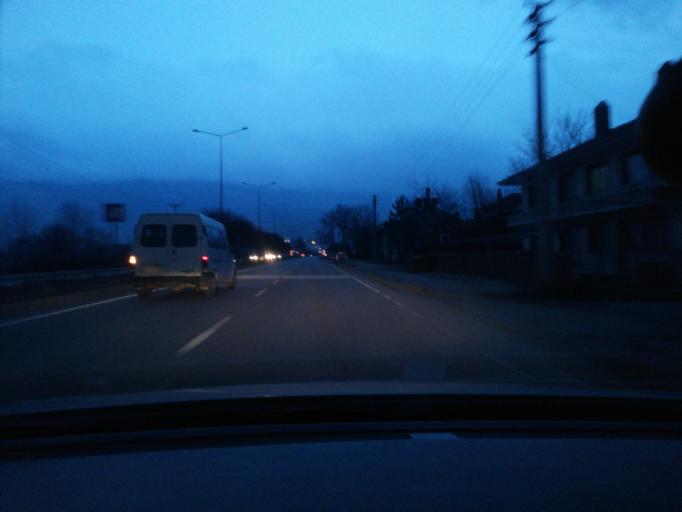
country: TR
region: Bolu
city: Bolu
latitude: 40.7069
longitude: 31.6171
